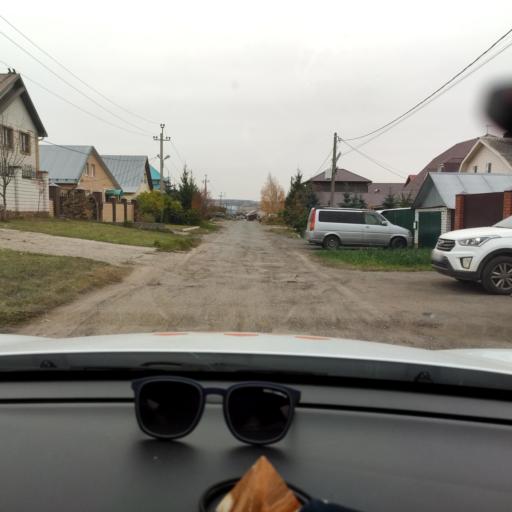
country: RU
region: Tatarstan
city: Vysokaya Gora
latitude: 55.8112
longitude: 49.2501
